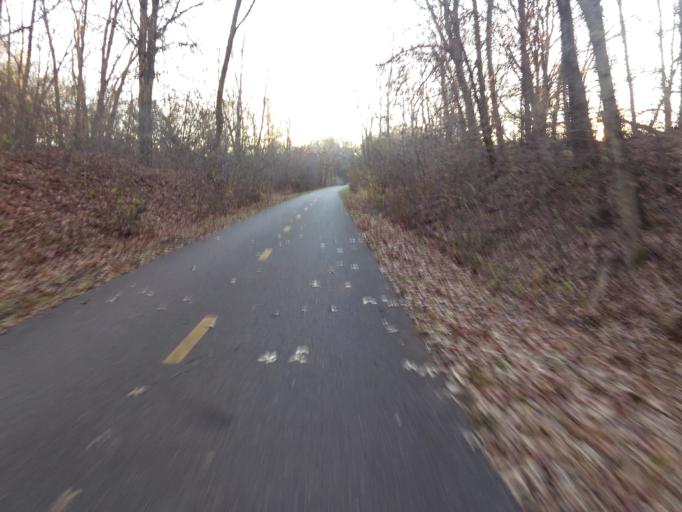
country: US
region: Minnesota
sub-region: Washington County
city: Grant
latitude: 45.0845
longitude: -92.8932
